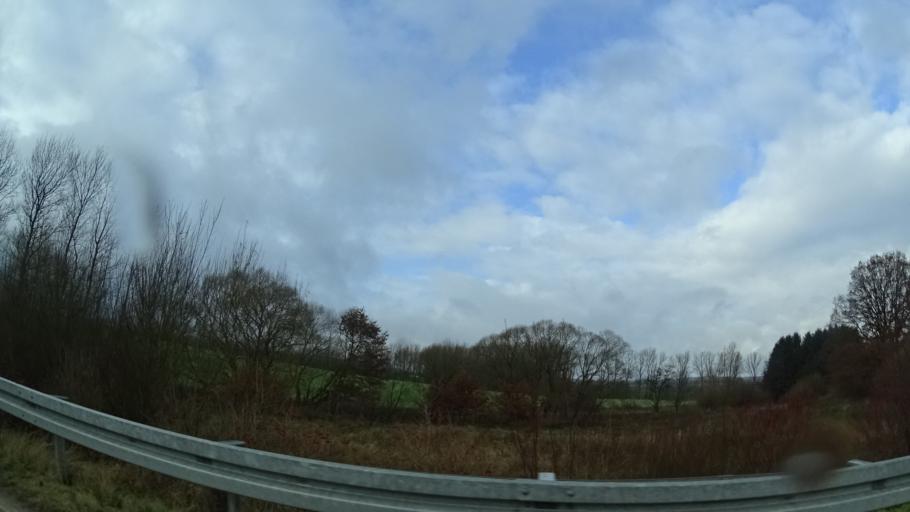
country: DE
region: Hesse
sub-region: Regierungsbezirk Kassel
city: Neuhof
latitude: 50.4298
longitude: 9.6044
